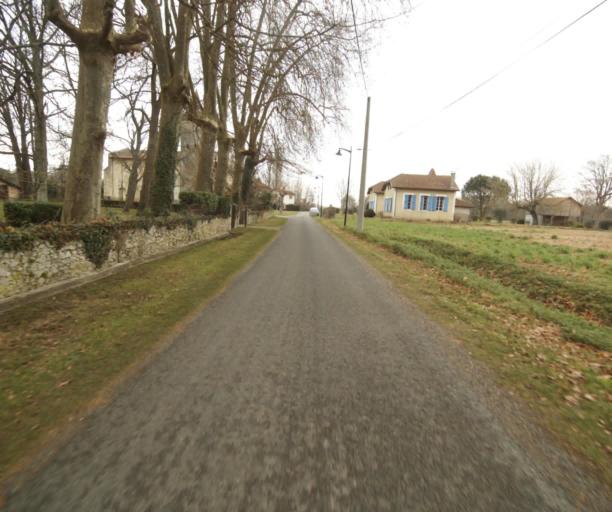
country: FR
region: Aquitaine
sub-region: Departement des Landes
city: Gabarret
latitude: 44.0072
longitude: -0.0245
